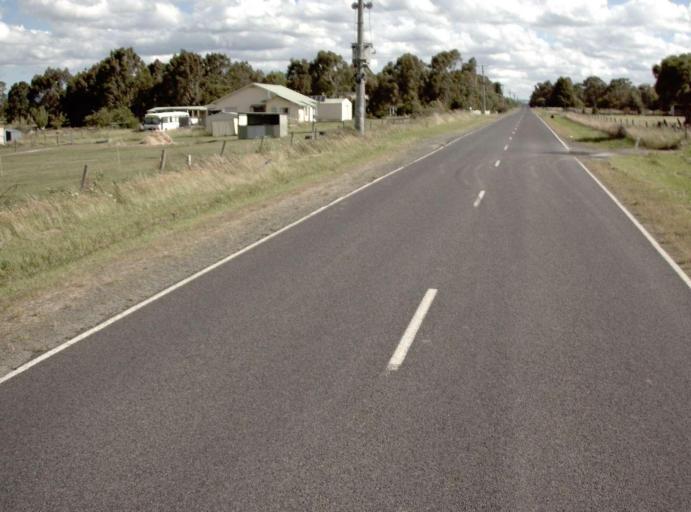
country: AU
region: Victoria
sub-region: Latrobe
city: Morwell
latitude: -38.2184
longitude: 146.3981
